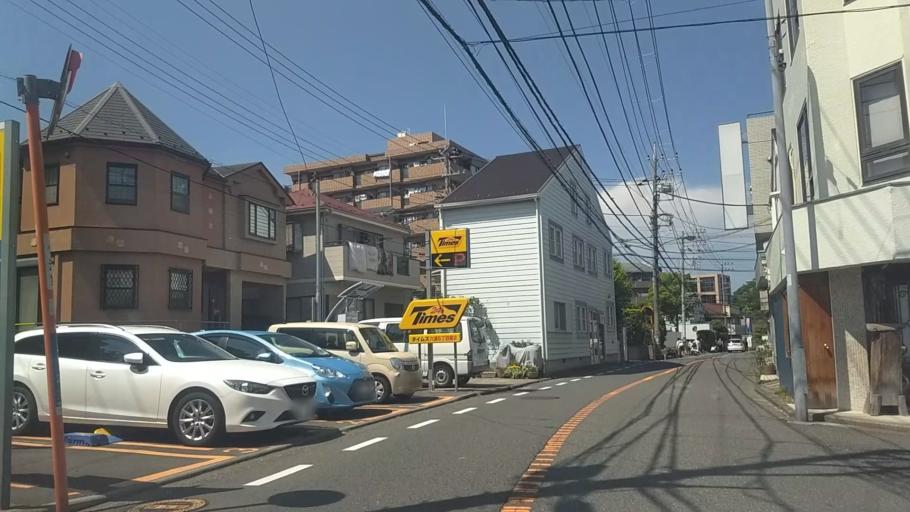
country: JP
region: Kanagawa
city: Zushi
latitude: 35.3239
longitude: 139.6115
